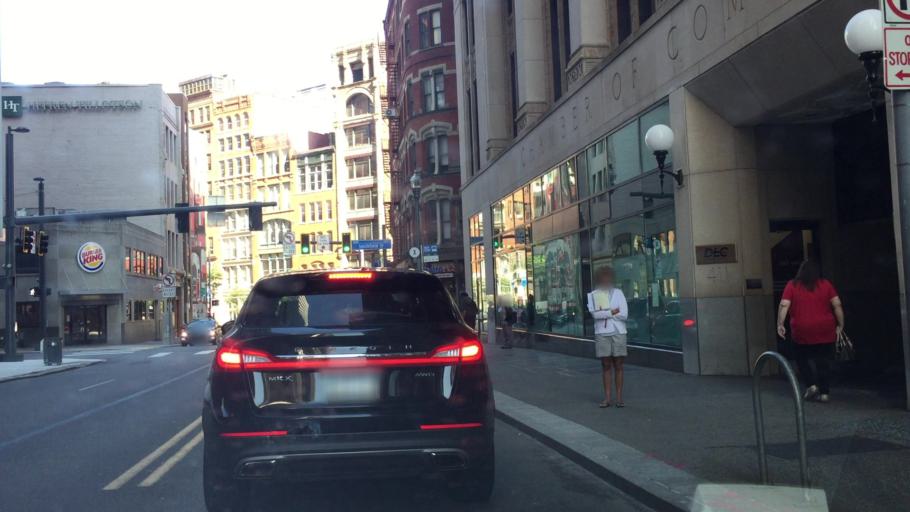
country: US
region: Pennsylvania
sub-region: Allegheny County
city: Pittsburgh
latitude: 40.4427
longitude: -79.9963
